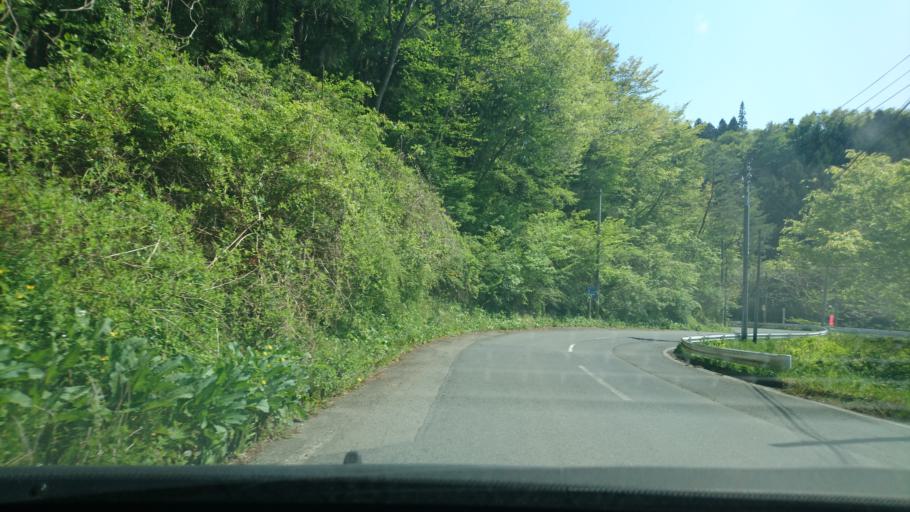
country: JP
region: Iwate
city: Ichinoseki
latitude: 38.9338
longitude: 141.2790
